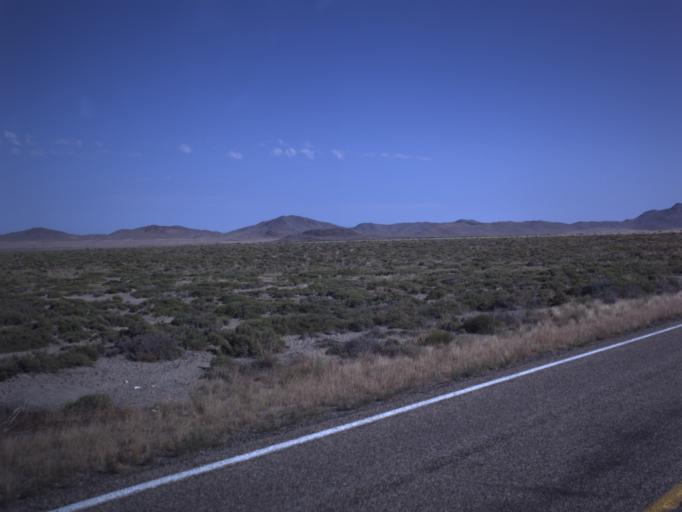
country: US
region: Utah
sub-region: Beaver County
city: Milford
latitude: 38.6426
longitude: -112.9831
